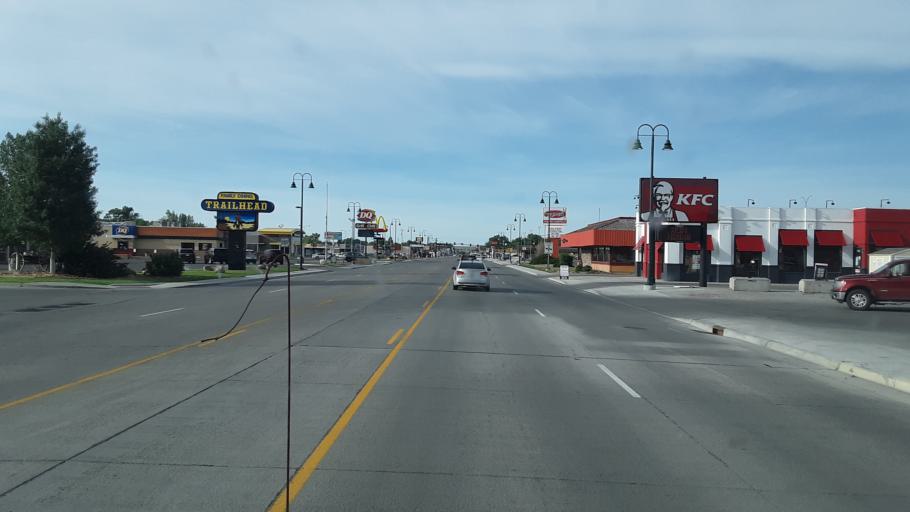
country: US
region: Wyoming
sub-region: Fremont County
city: Riverton
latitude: 43.0335
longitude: -108.3807
